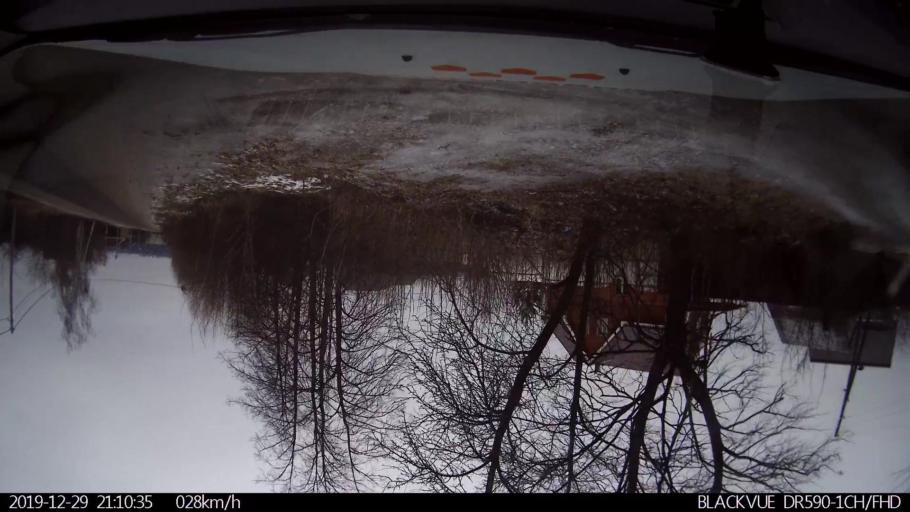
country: RU
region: Nizjnij Novgorod
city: Afonino
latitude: 56.2234
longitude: 44.0394
